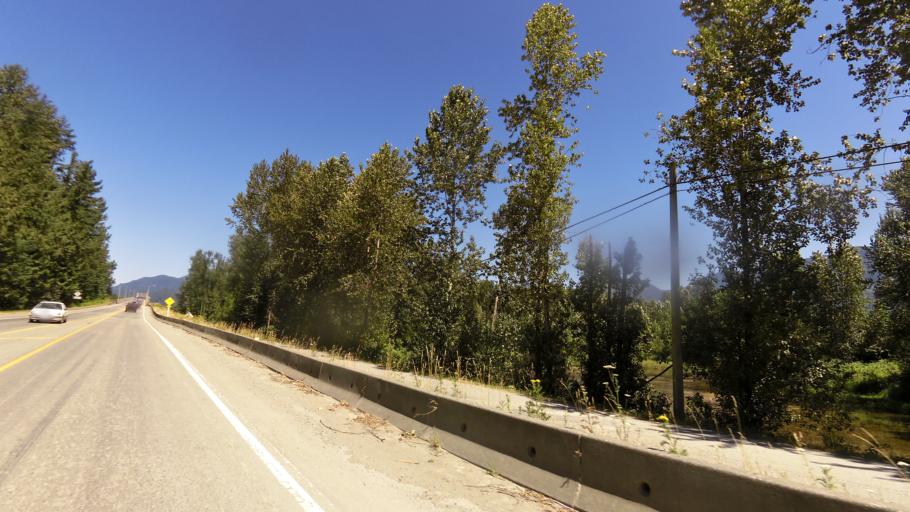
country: CA
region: British Columbia
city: Agassiz
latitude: 49.2001
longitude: -121.7779
